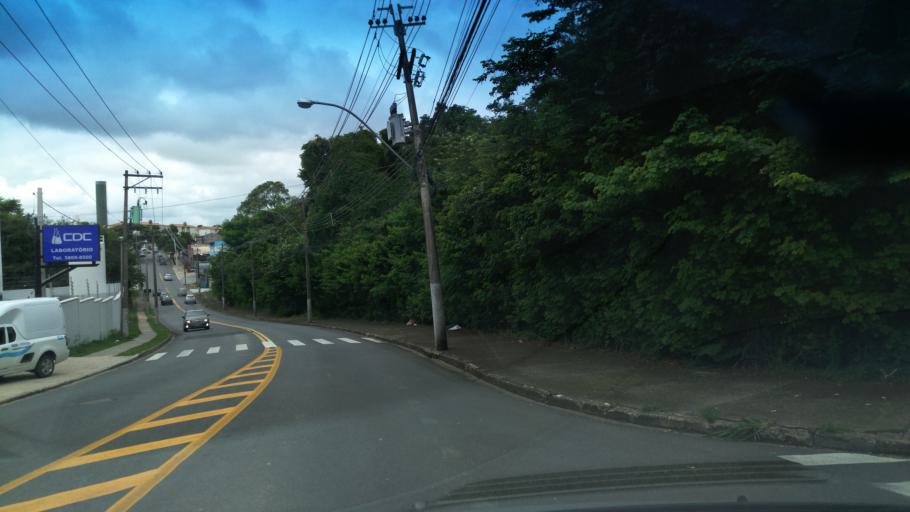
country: BR
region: Sao Paulo
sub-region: Valinhos
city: Valinhos
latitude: -22.9711
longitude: -46.9879
